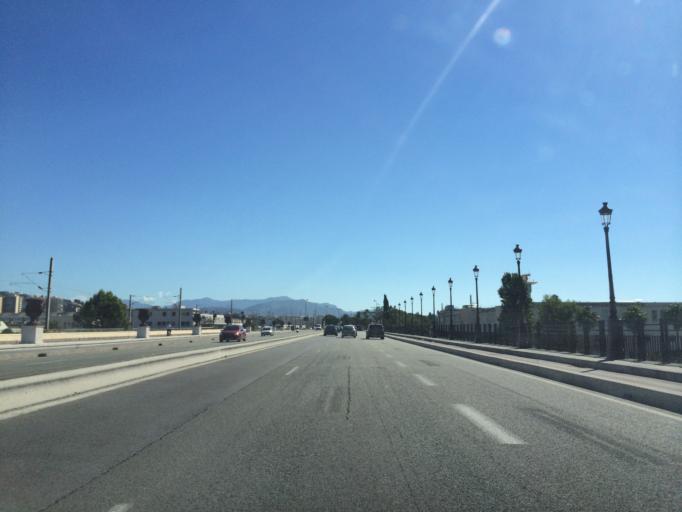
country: FR
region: Provence-Alpes-Cote d'Azur
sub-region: Departement des Alpes-Maritimes
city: Saint-Laurent-du-Var
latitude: 43.6639
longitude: 7.1993
